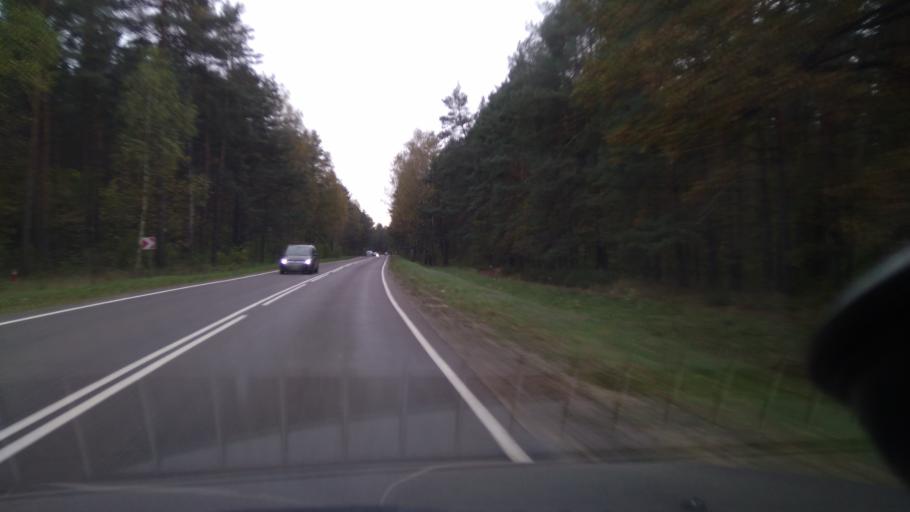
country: BY
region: Minsk
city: Svislach
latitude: 53.6408
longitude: 27.9078
